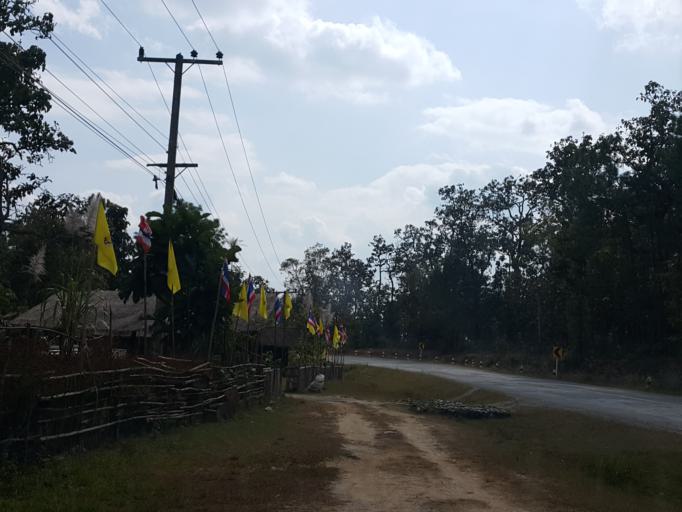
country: TH
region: Chiang Mai
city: Om Koi
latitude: 17.8480
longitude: 98.3707
